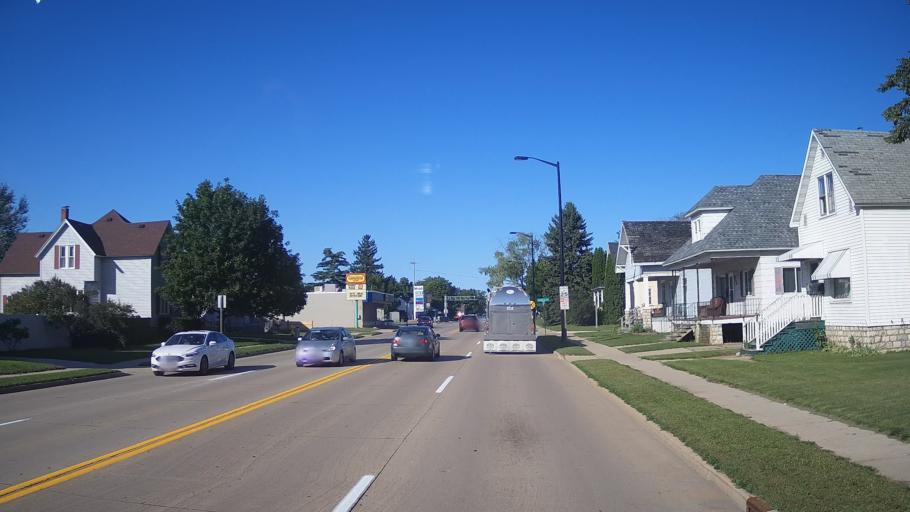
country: US
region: Wisconsin
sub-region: Marinette County
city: Marinette
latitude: 45.0947
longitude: -87.6448
